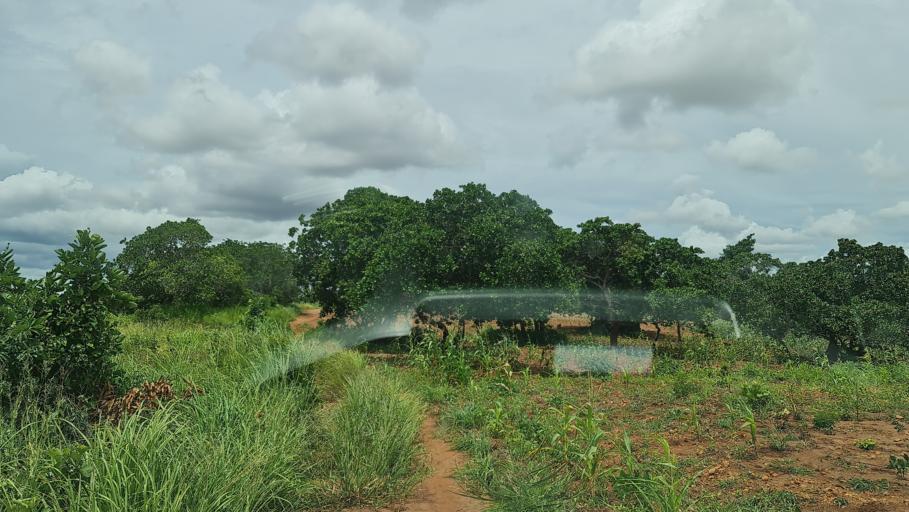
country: MZ
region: Nampula
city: Nacala
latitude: -14.7781
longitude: 39.9934
